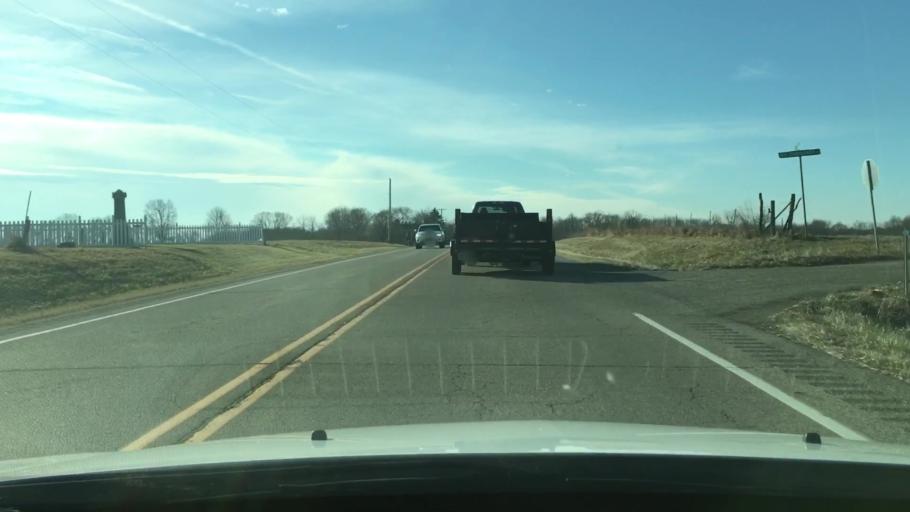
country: US
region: Illinois
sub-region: Marshall County
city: Toluca
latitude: 41.0762
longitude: -89.2098
